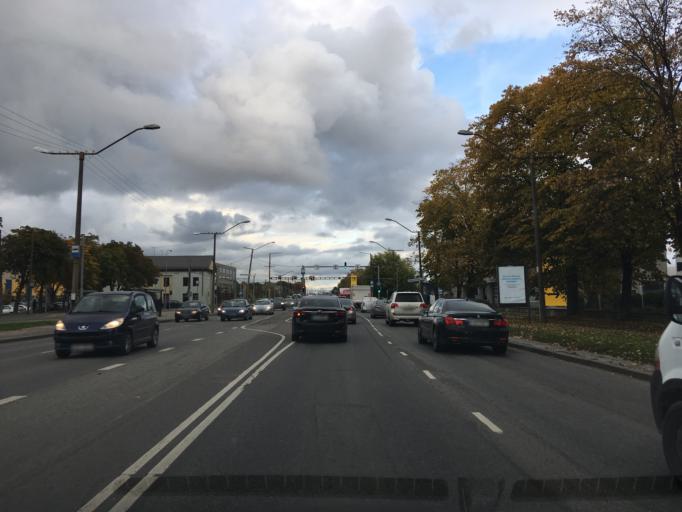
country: EE
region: Harju
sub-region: Tallinna linn
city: Tallinn
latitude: 59.4261
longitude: 24.8069
